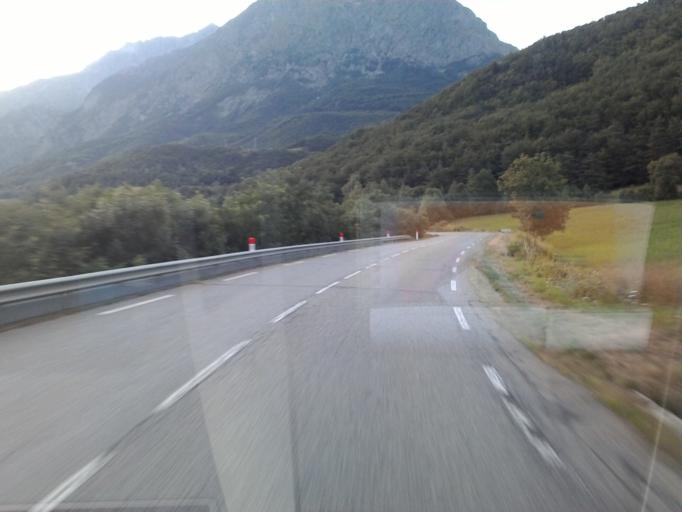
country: FR
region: Provence-Alpes-Cote d'Azur
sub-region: Departement des Hautes-Alpes
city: Saint-Bonnet-en-Champsaur
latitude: 44.7707
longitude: 6.0195
